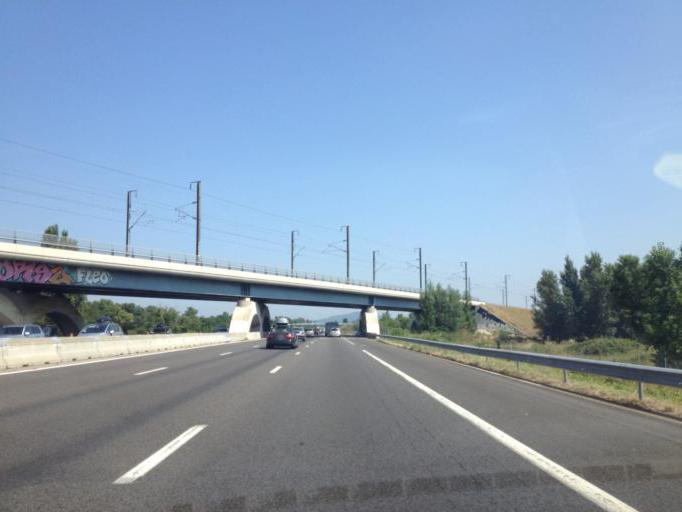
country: FR
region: Rhone-Alpes
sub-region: Departement de la Drome
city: Pierrelatte
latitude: 44.3770
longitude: 4.7326
